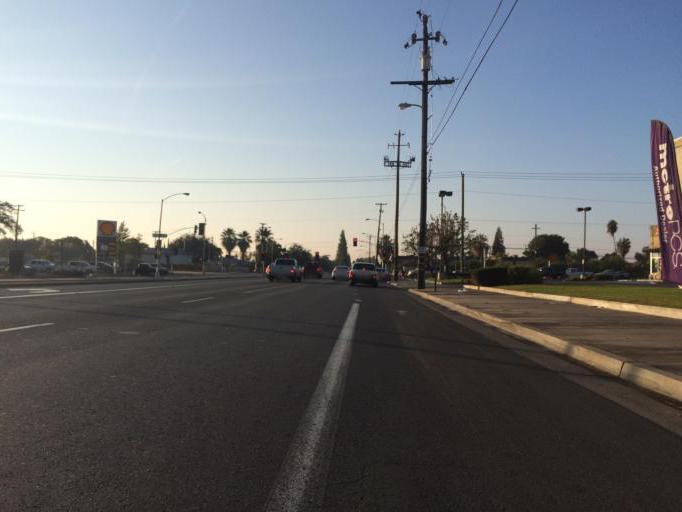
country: US
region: California
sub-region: Fresno County
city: Fresno
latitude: 36.7804
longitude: -119.7727
